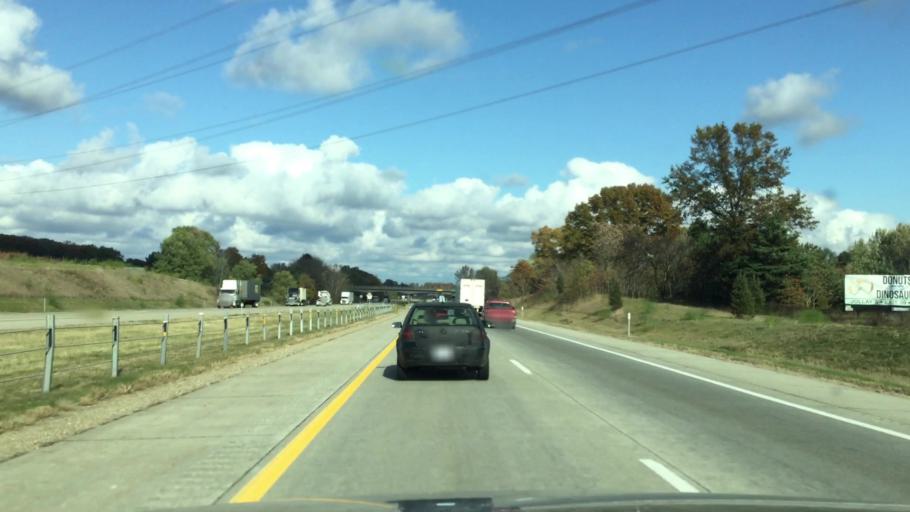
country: US
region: Michigan
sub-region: Berrien County
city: Coloma
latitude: 42.1594
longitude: -86.3334
